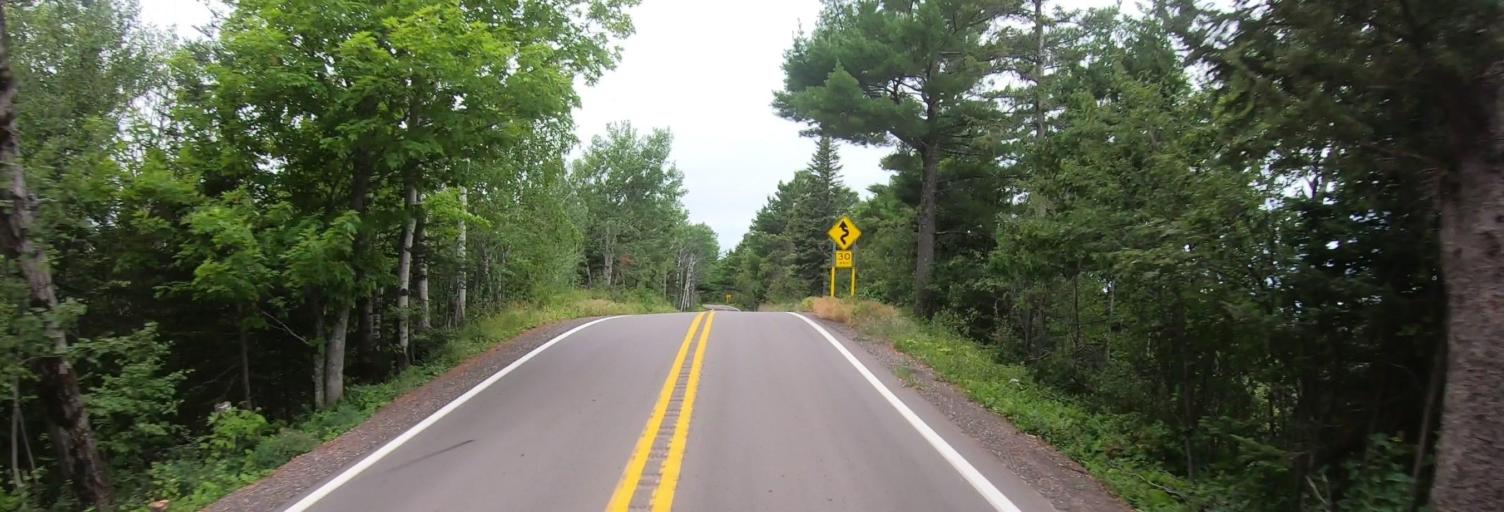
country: US
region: Michigan
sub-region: Keweenaw County
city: Eagle River
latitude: 47.4600
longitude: -88.1191
